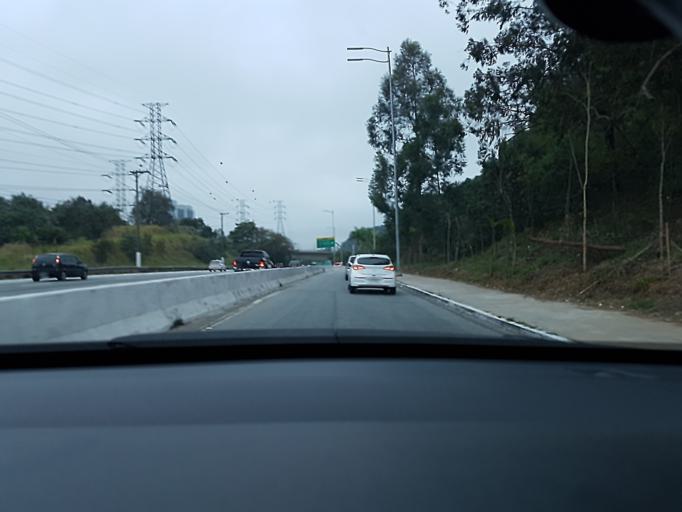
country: BR
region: Sao Paulo
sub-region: Taboao Da Serra
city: Taboao da Serra
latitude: -23.6313
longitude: -46.7179
